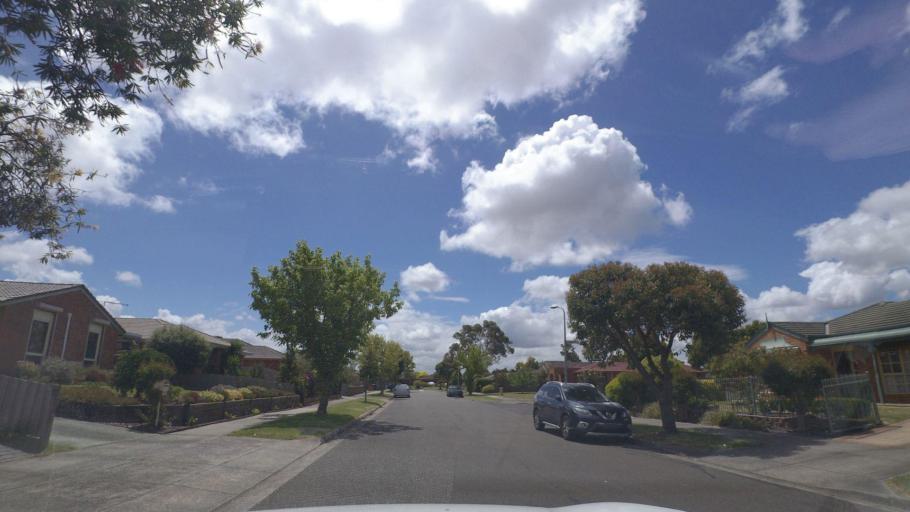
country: AU
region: Victoria
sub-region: Knox
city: Knoxfield
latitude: -37.9119
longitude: 145.2633
